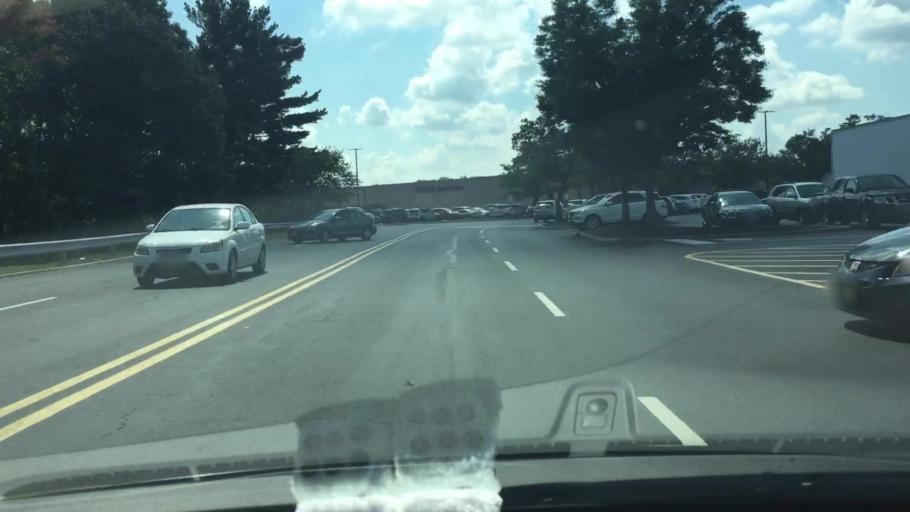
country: US
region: New Jersey
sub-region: Camden County
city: Glendora
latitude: 39.8303
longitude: -75.0958
